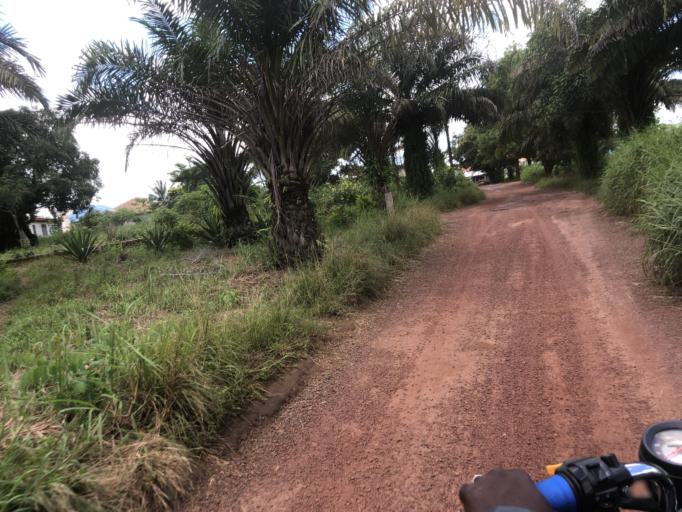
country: SL
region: Northern Province
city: Makeni
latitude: 8.8613
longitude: -12.0457
